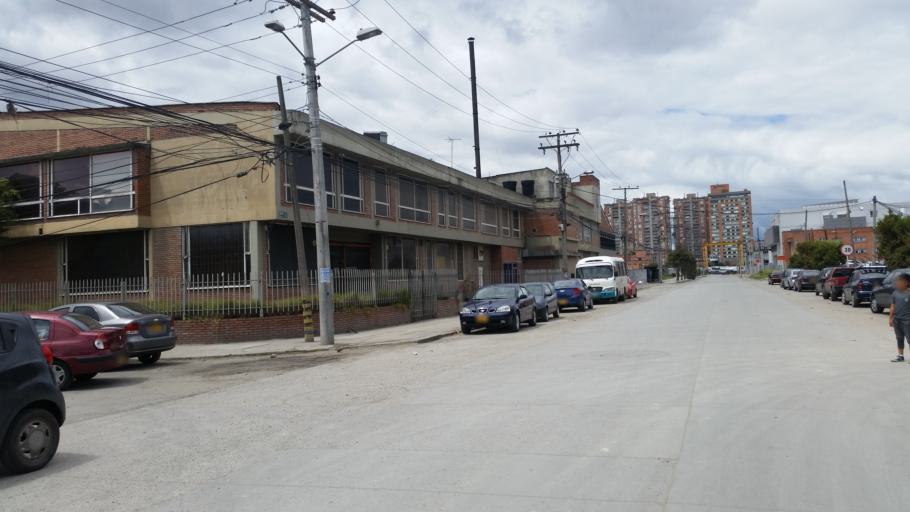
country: CO
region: Bogota D.C.
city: Bogota
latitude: 4.6373
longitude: -74.1093
